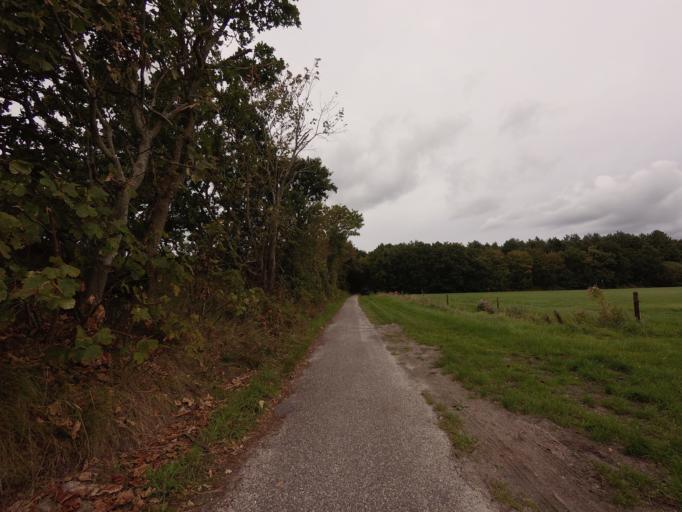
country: NL
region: Friesland
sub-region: Gemeente Ameland
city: Nes
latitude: 53.4501
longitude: 5.7132
